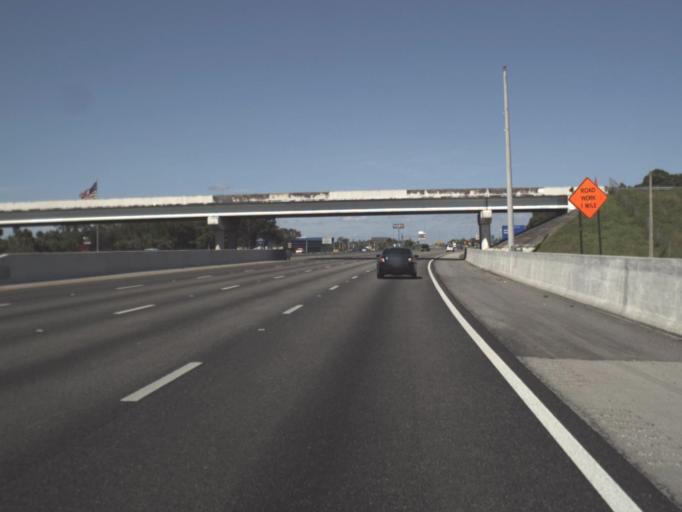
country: US
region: Florida
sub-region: Lee County
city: Tice
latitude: 26.6698
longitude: -81.7995
